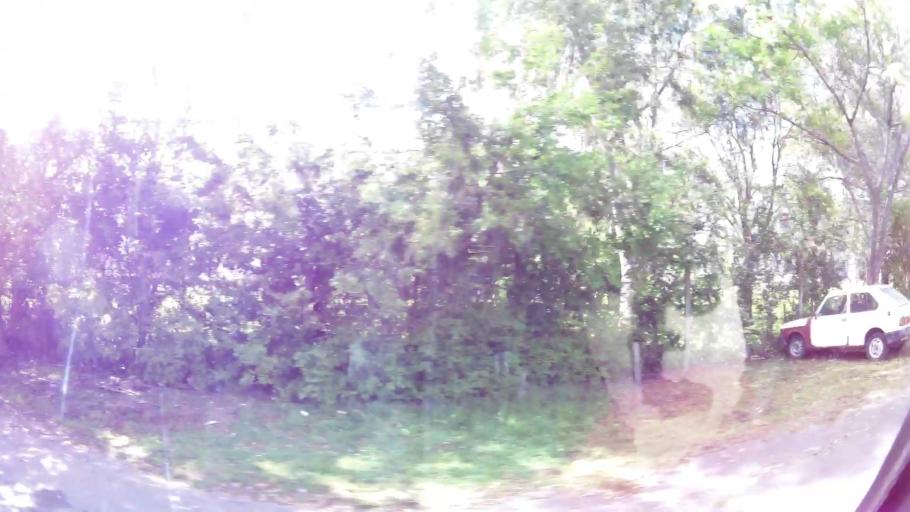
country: AR
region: Buenos Aires
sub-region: Partido de Quilmes
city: Quilmes
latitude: -34.7982
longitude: -58.1564
